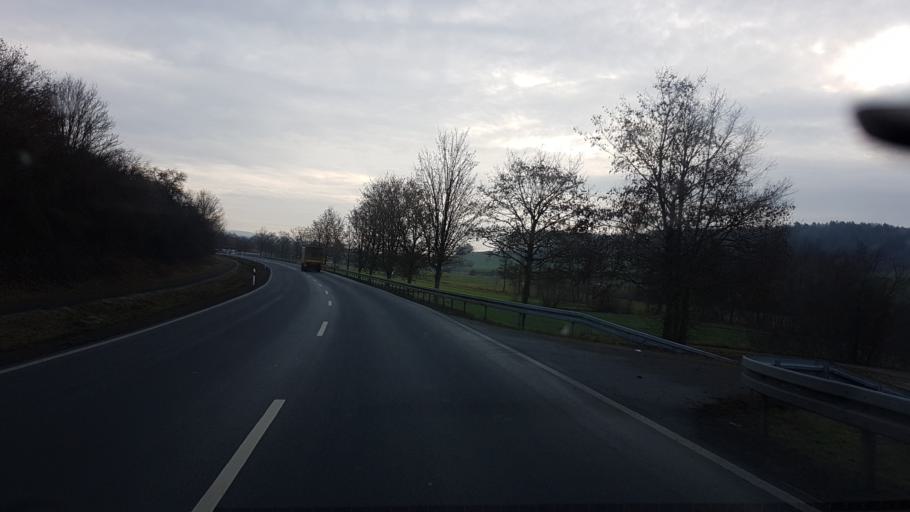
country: DE
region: Bavaria
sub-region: Regierungsbezirk Unterfranken
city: Pfarrweisach
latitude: 50.1653
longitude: 10.7212
